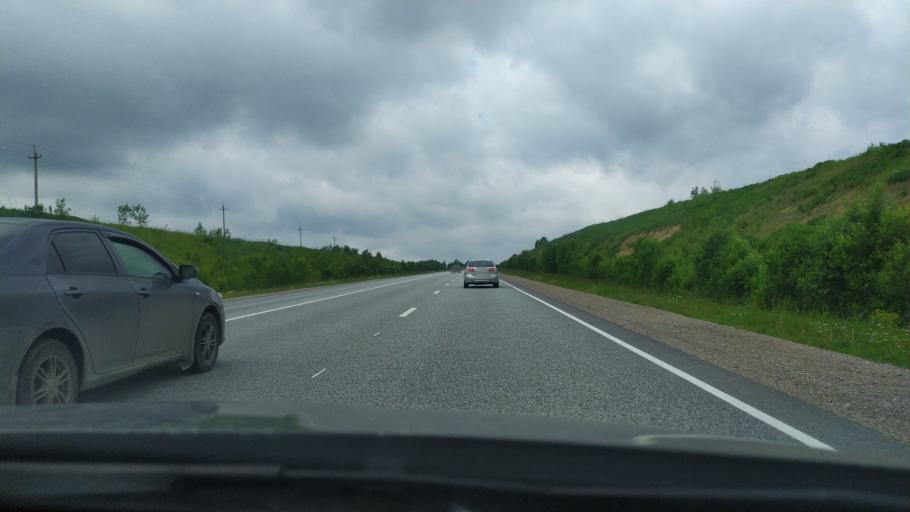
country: RU
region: Perm
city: Verkhnechusovskiye Gorodki
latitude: 58.2652
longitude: 57.3274
